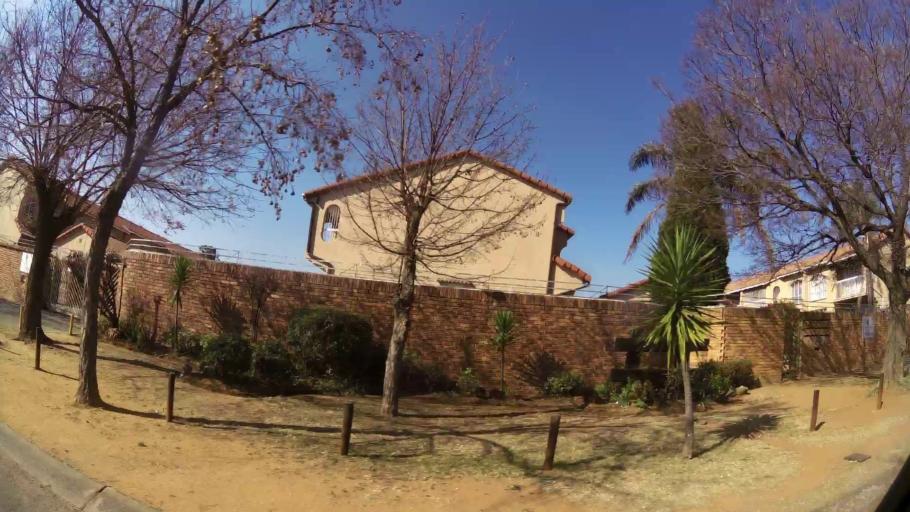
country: ZA
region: Gauteng
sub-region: City of Johannesburg Metropolitan Municipality
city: Johannesburg
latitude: -26.2582
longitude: 27.9942
